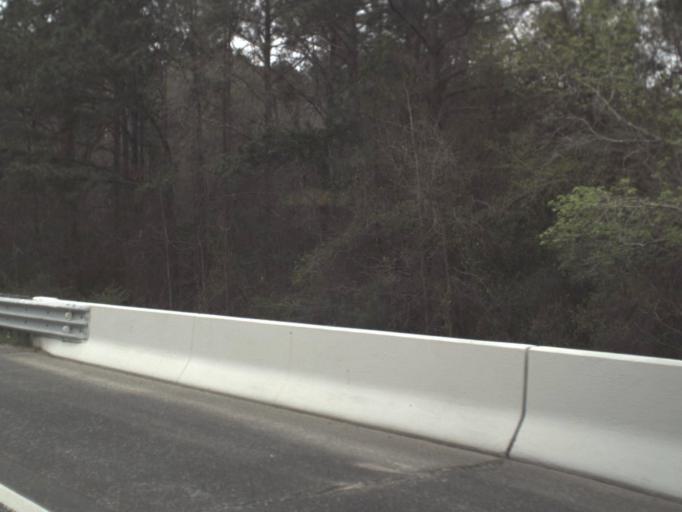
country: US
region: Florida
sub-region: Calhoun County
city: Blountstown
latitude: 30.4448
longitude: -85.1829
